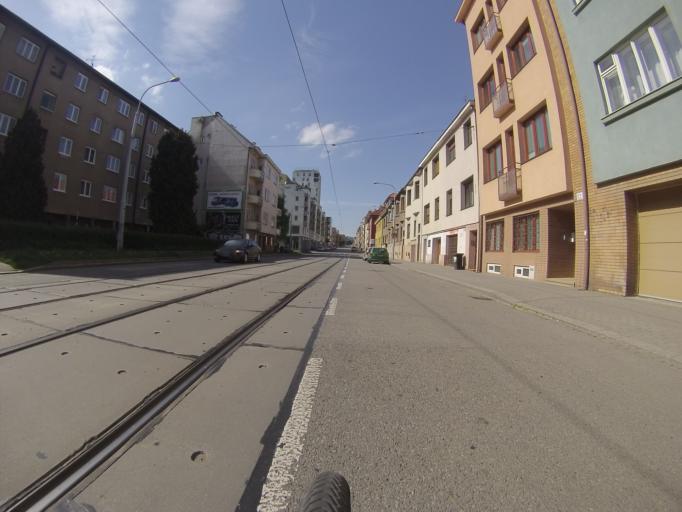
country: CZ
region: South Moravian
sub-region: Mesto Brno
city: Brno
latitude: 49.2198
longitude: 16.5867
